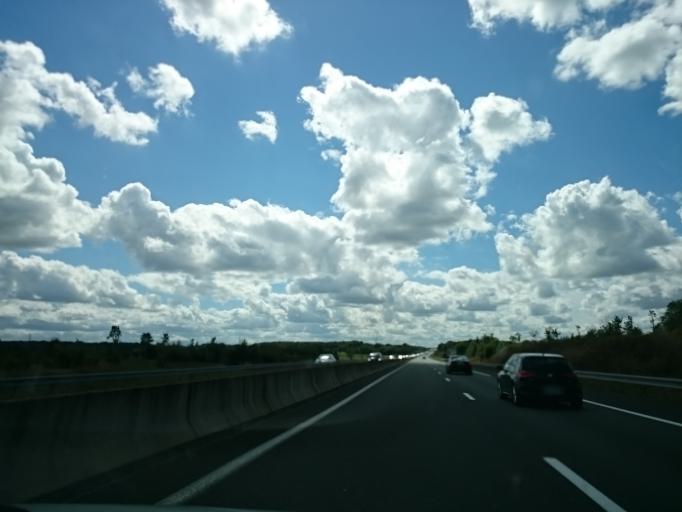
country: FR
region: Pays de la Loire
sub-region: Departement de Maine-et-Loire
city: Saint-Lambert-la-Potherie
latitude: 47.4807
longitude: -0.6673
